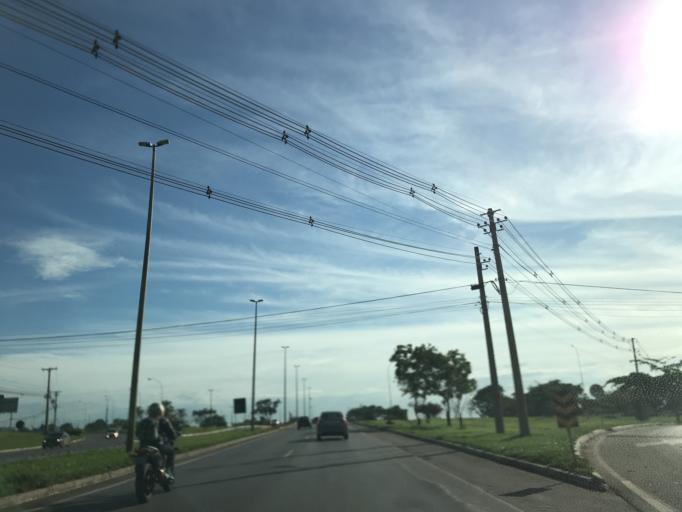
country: BR
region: Federal District
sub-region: Brasilia
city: Brasilia
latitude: -15.8633
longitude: -47.9591
